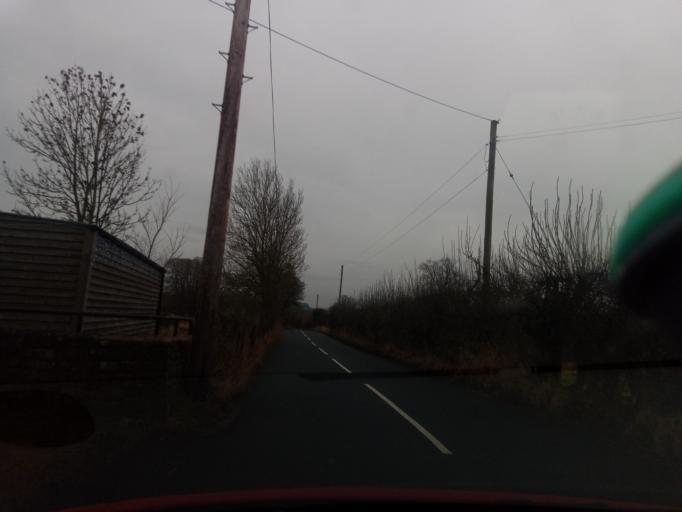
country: GB
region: England
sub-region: Northumberland
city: Birtley
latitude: 55.1463
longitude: -2.2682
